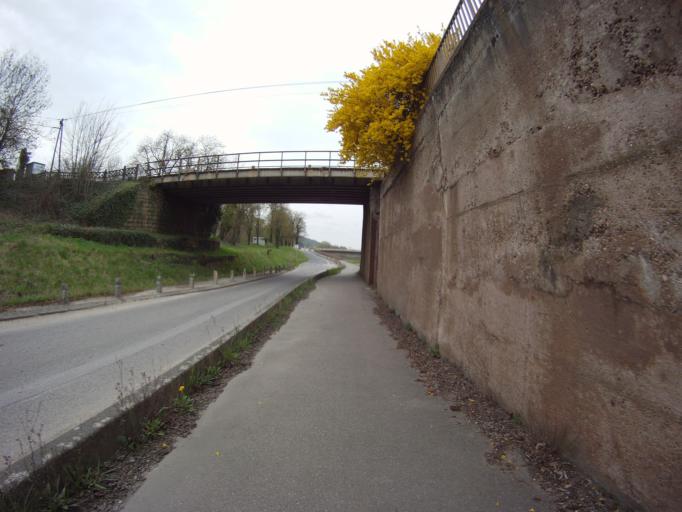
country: FR
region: Lorraine
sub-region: Departement de Meurthe-et-Moselle
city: Pont-Saint-Vincent
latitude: 48.6071
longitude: 6.1037
